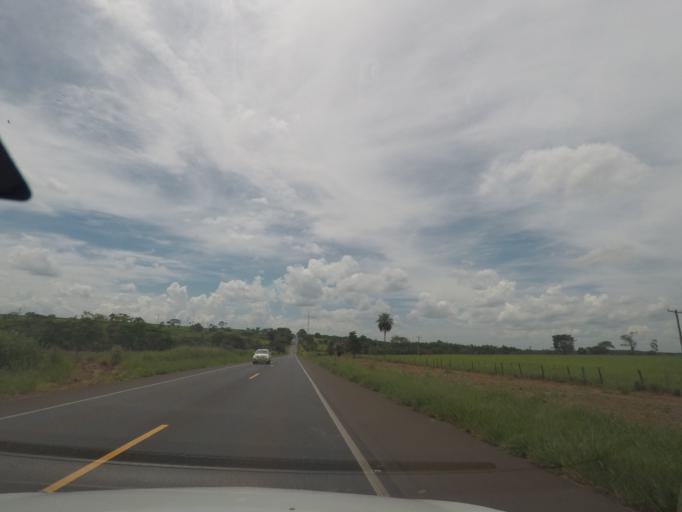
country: BR
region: Sao Paulo
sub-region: Barretos
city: Barretos
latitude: -20.4301
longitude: -48.6278
